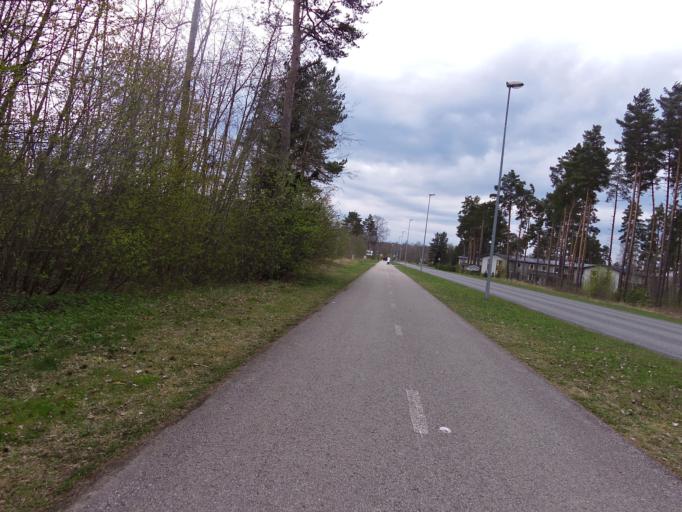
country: EE
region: Harju
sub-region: Kiili vald
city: Kiili
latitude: 59.3605
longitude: 24.8139
